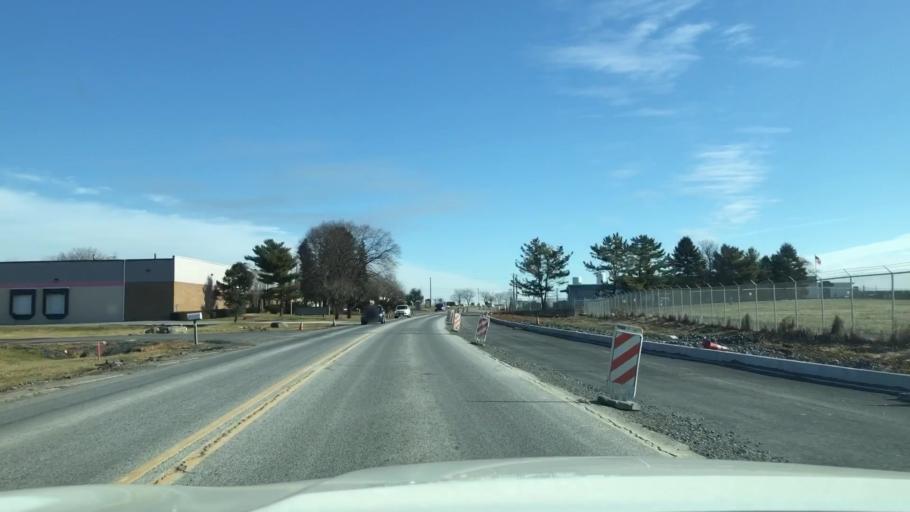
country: US
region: Pennsylvania
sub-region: Lehigh County
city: Catasauqua
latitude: 40.6604
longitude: -75.4408
